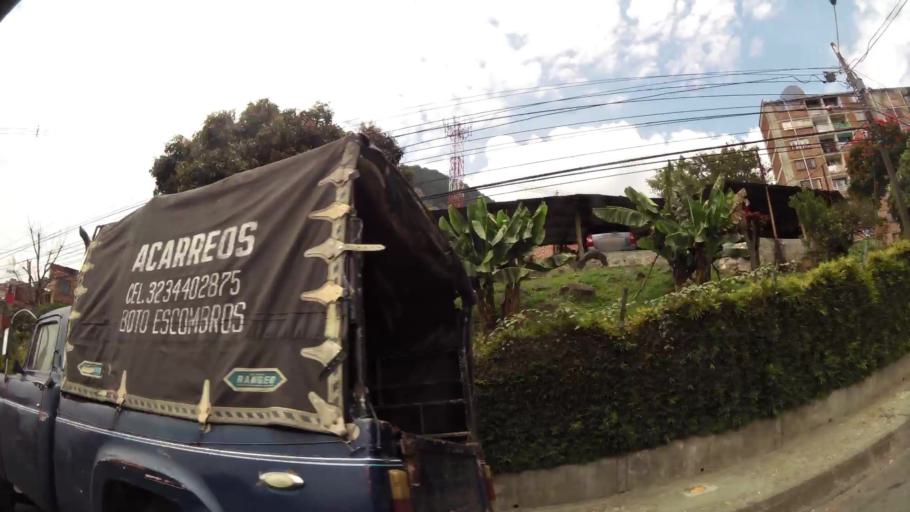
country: CO
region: Antioquia
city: Bello
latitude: 6.3048
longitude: -75.5818
